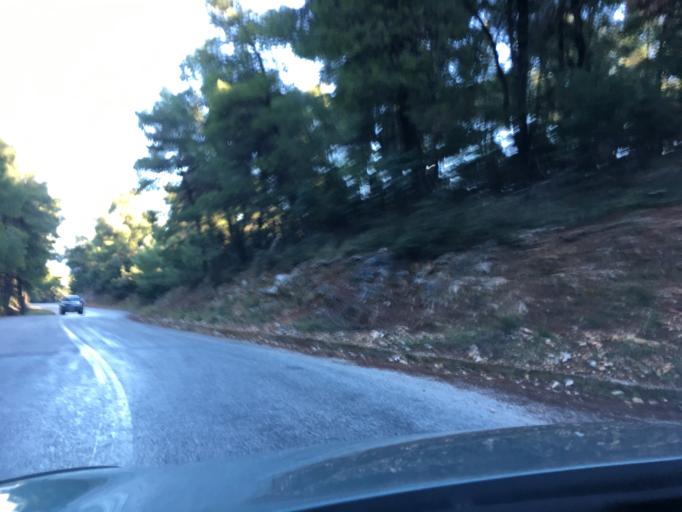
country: GR
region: Thessaly
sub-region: Nomos Magnisias
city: Skopelos
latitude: 39.0942
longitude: 23.7171
